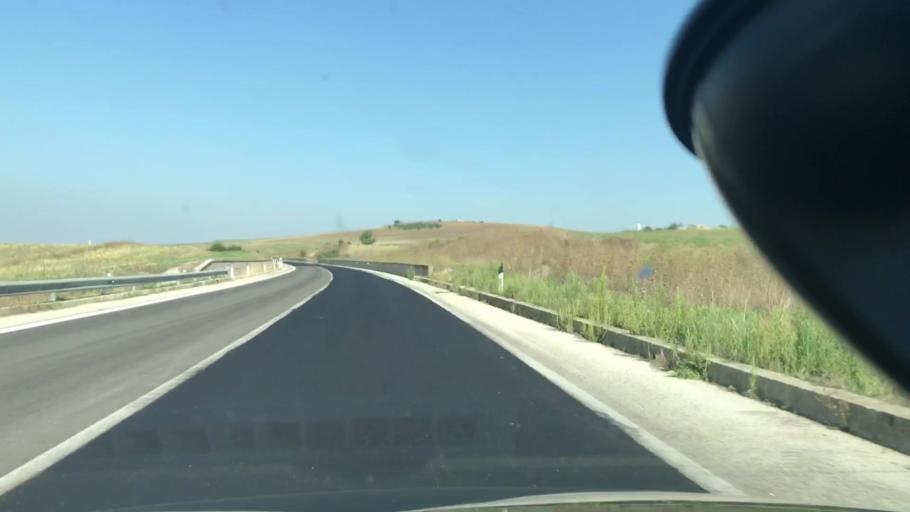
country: IT
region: Apulia
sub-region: Provincia di Barletta - Andria - Trani
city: Spinazzola
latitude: 40.9192
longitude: 16.0993
